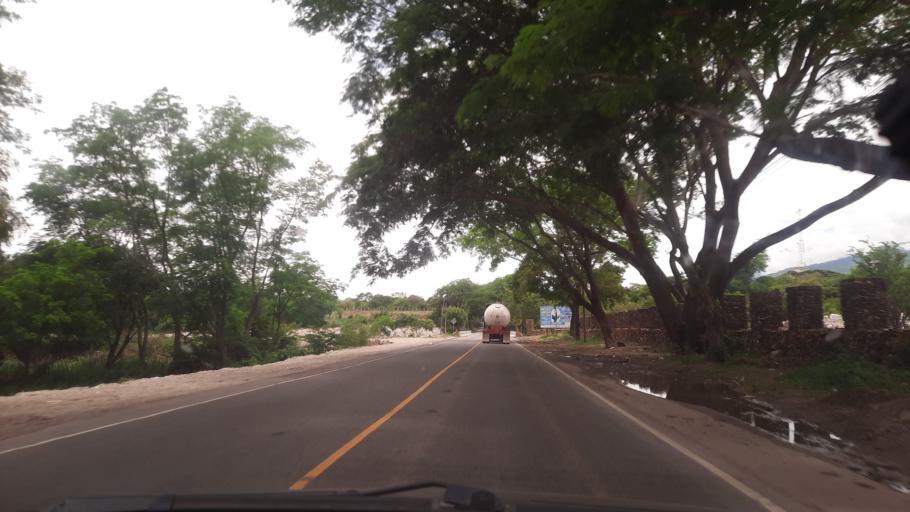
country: GT
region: Zacapa
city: Rio Hondo
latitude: 15.0717
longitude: -89.5082
